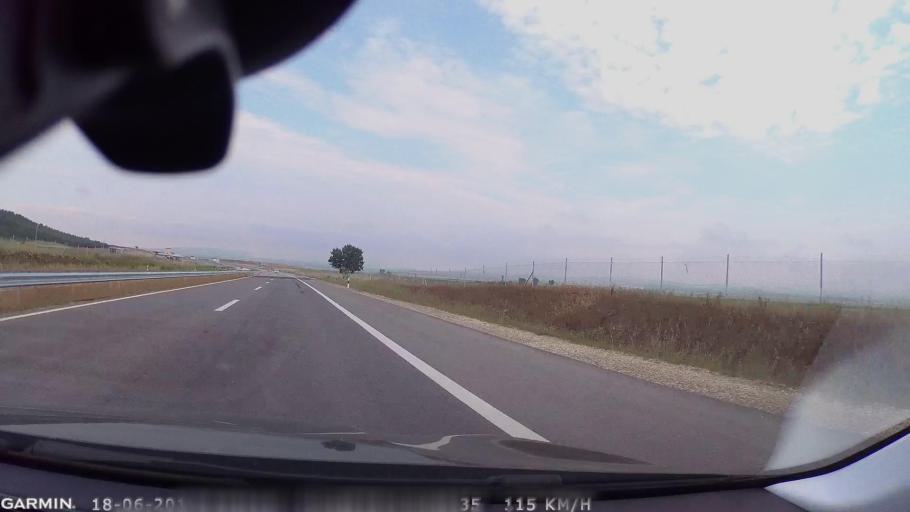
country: MK
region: Sveti Nikole
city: Sveti Nikole
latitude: 41.8080
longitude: 22.0615
